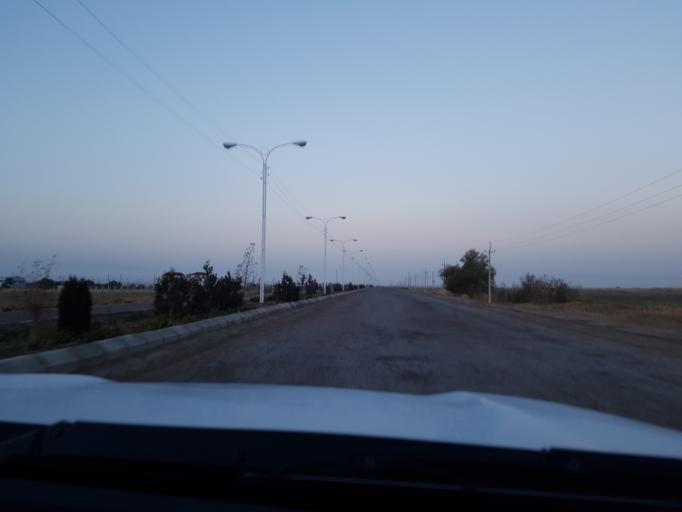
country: TM
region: Dasoguz
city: Koeneuergench
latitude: 41.7426
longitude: 58.7137
